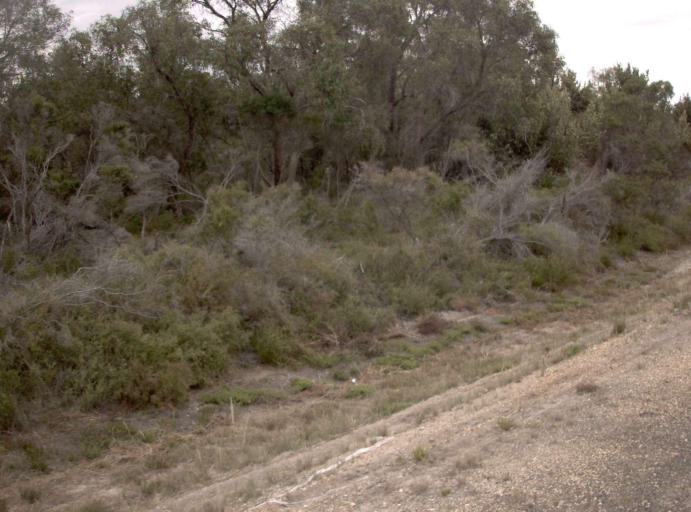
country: AU
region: Victoria
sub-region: Wellington
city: Sale
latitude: -38.1739
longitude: 147.3823
